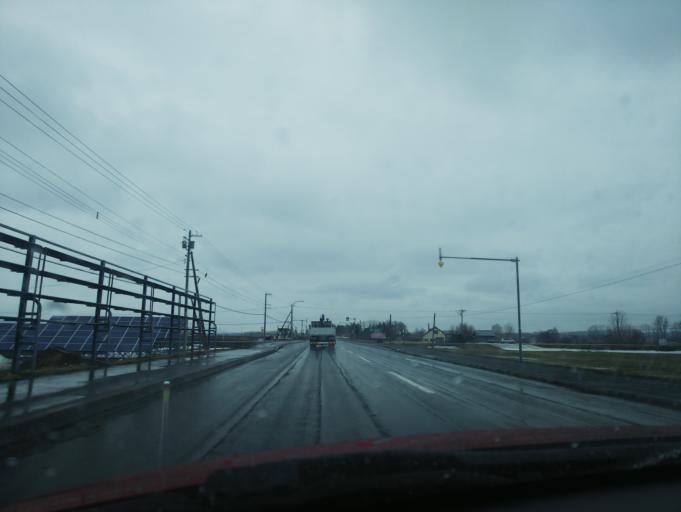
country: JP
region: Hokkaido
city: Nayoro
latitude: 44.2146
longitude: 142.3949
